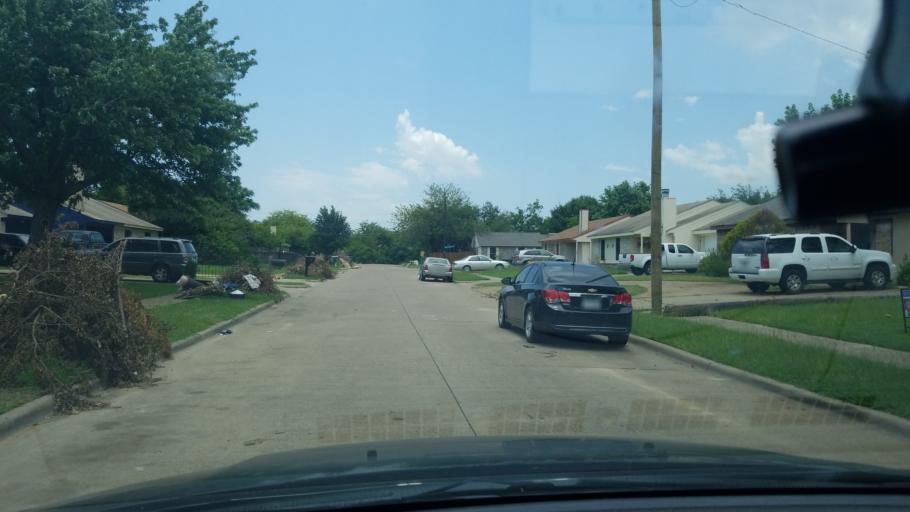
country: US
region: Texas
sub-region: Dallas County
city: Balch Springs
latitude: 32.7147
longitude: -96.6629
